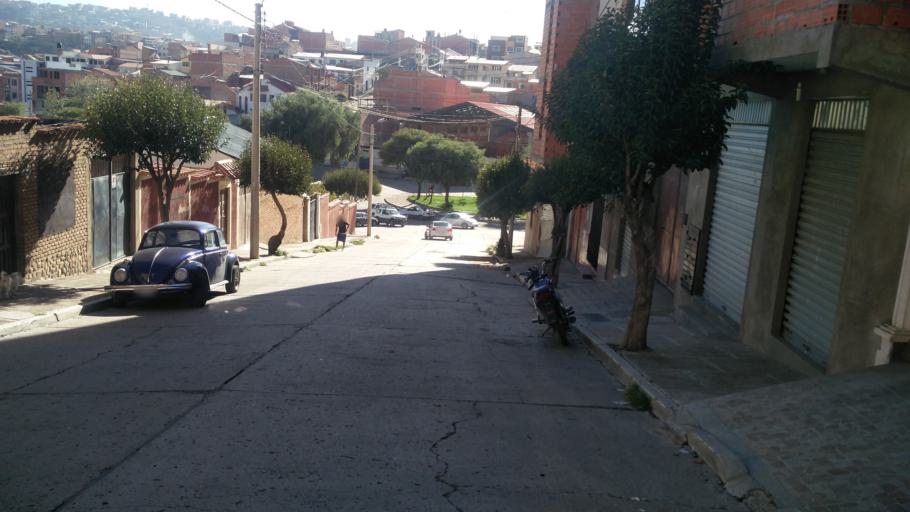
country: BO
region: Chuquisaca
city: Sucre
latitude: -19.0325
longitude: -65.2639
